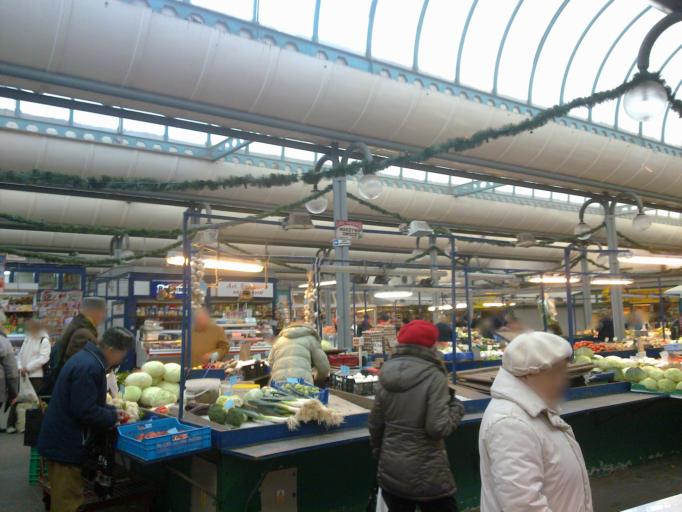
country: PL
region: Pomeranian Voivodeship
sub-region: Gdynia
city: Gdynia
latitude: 54.5223
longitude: 18.5339
